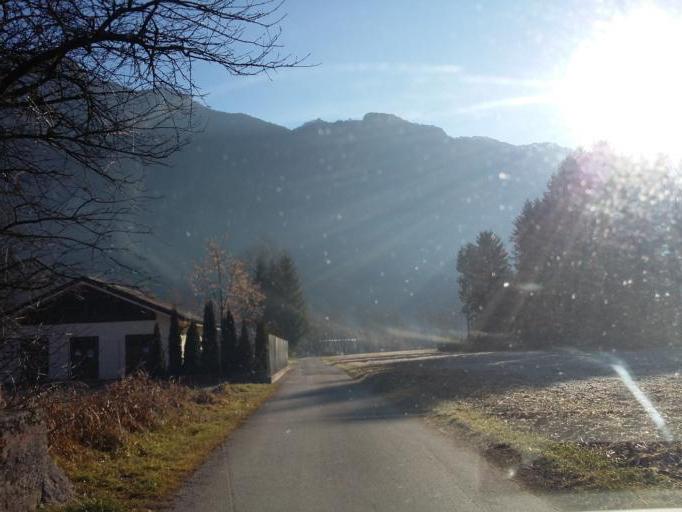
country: IT
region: Trentino-Alto Adige
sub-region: Provincia di Trento
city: Lodrone-Darzo
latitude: 45.8229
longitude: 10.5442
